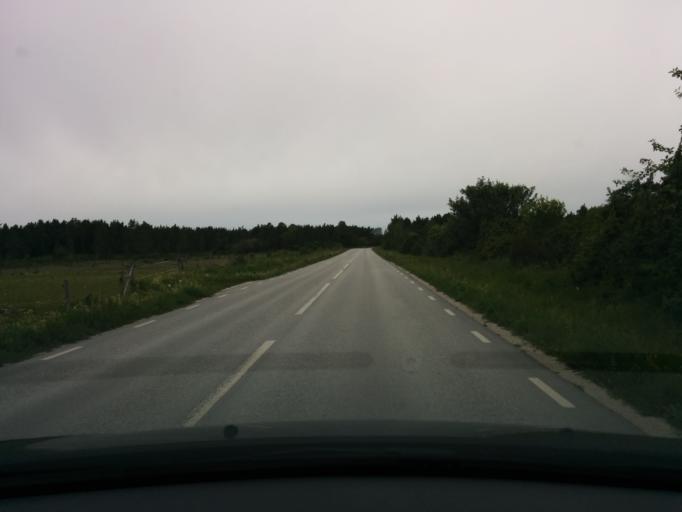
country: SE
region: Gotland
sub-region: Gotland
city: Slite
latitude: 57.6745
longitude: 18.7709
